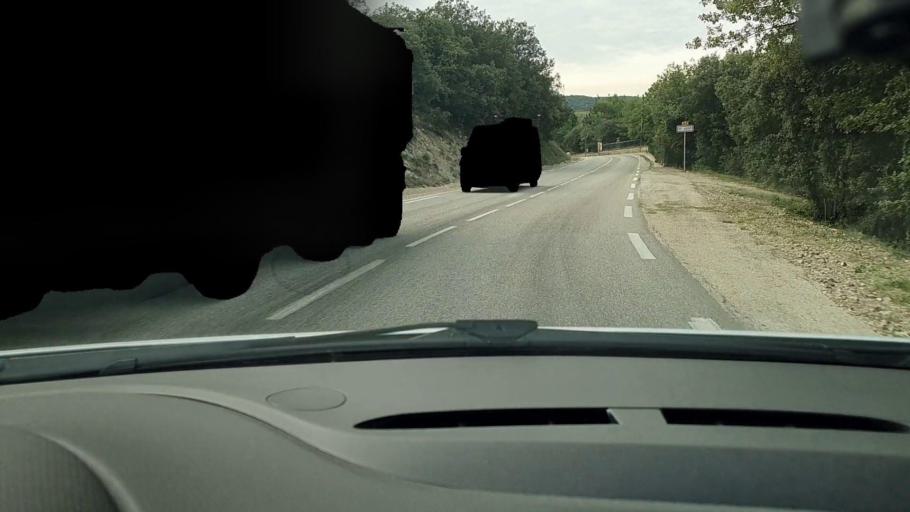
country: FR
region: Languedoc-Roussillon
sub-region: Departement du Gard
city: Mons
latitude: 44.1134
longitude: 4.2245
